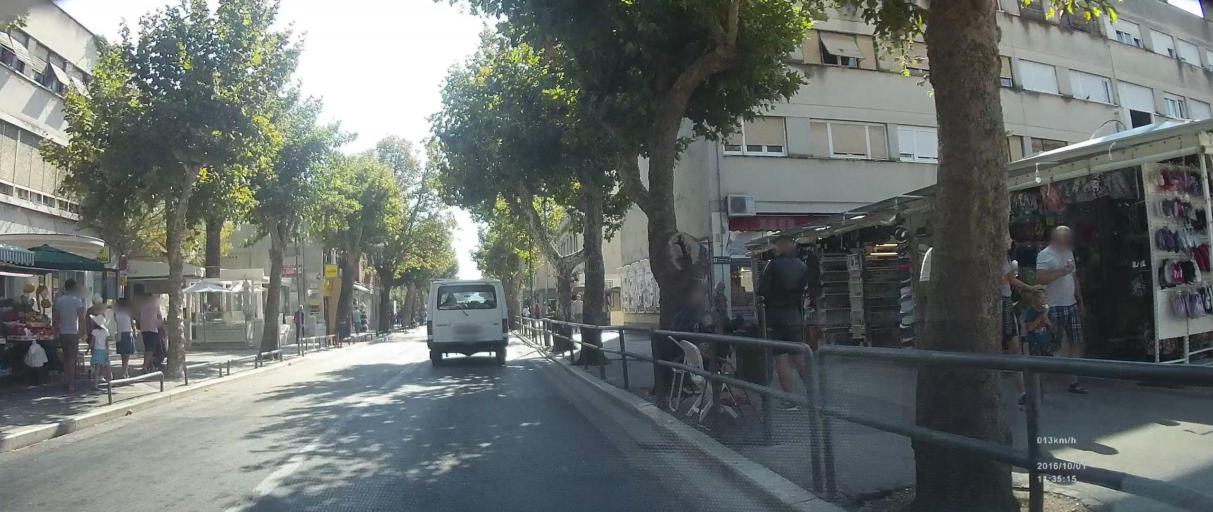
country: HR
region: Splitsko-Dalmatinska
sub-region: Grad Omis
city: Omis
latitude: 43.4444
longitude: 16.6919
